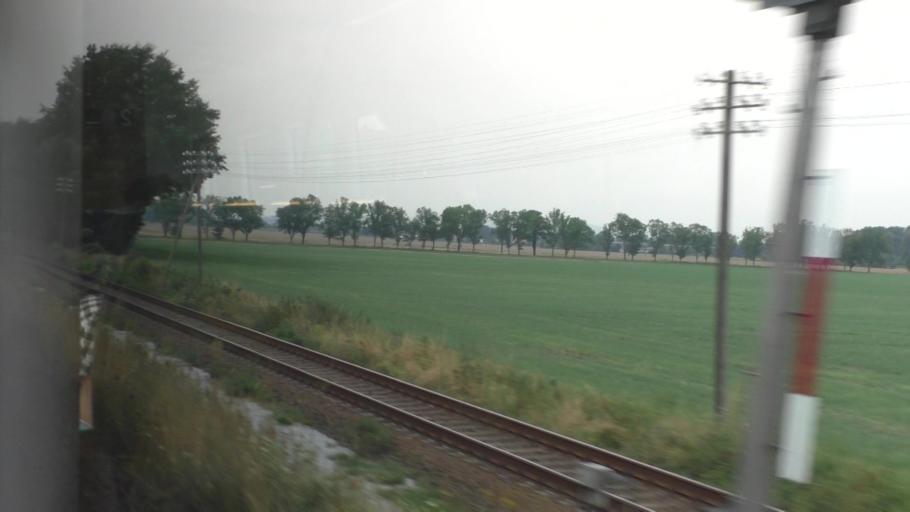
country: DE
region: Saxony
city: Horka
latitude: 51.2941
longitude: 14.9025
